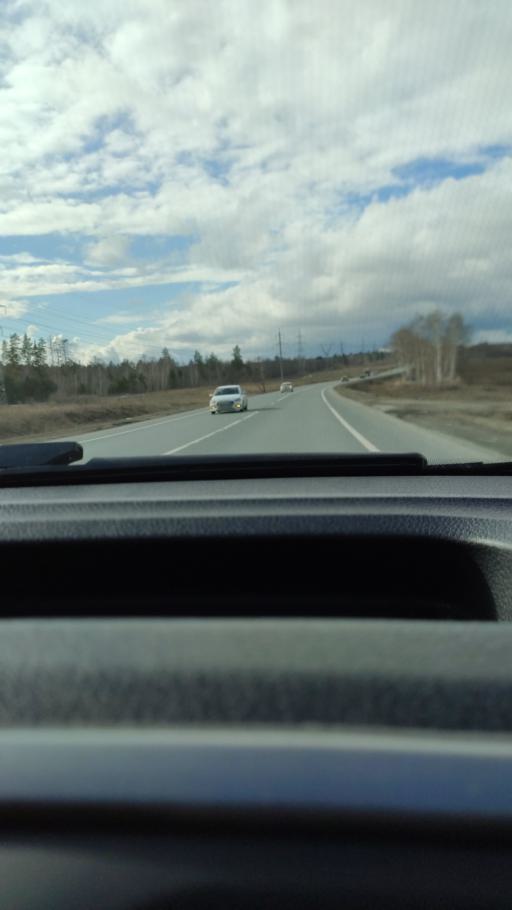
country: RU
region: Samara
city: Kurumoch
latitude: 53.4920
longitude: 49.9728
